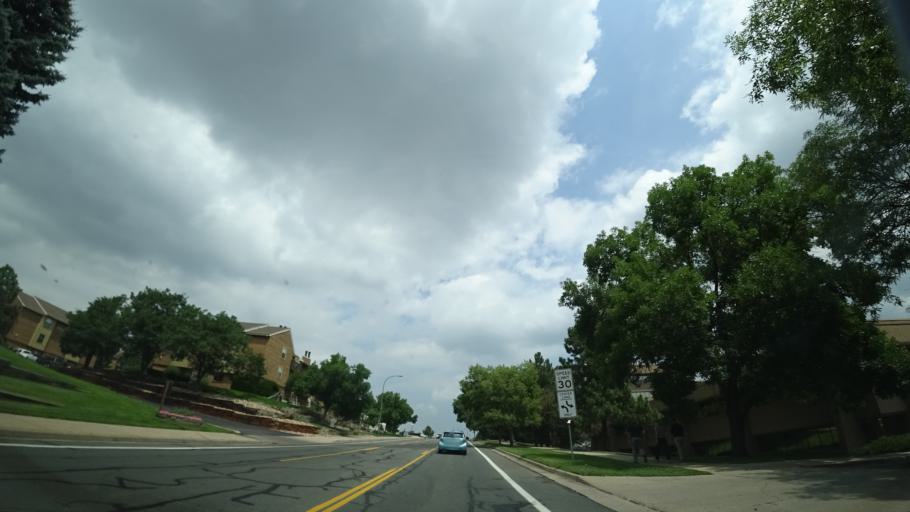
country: US
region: Colorado
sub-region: Jefferson County
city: West Pleasant View
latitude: 39.7190
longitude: -105.1352
